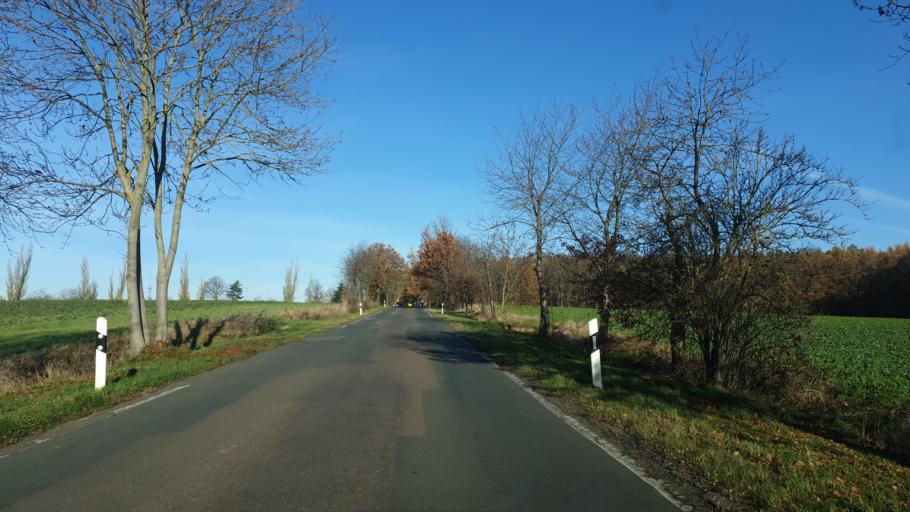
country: DE
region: Saxony-Anhalt
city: Wetterzeube
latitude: 51.0172
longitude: 12.0013
